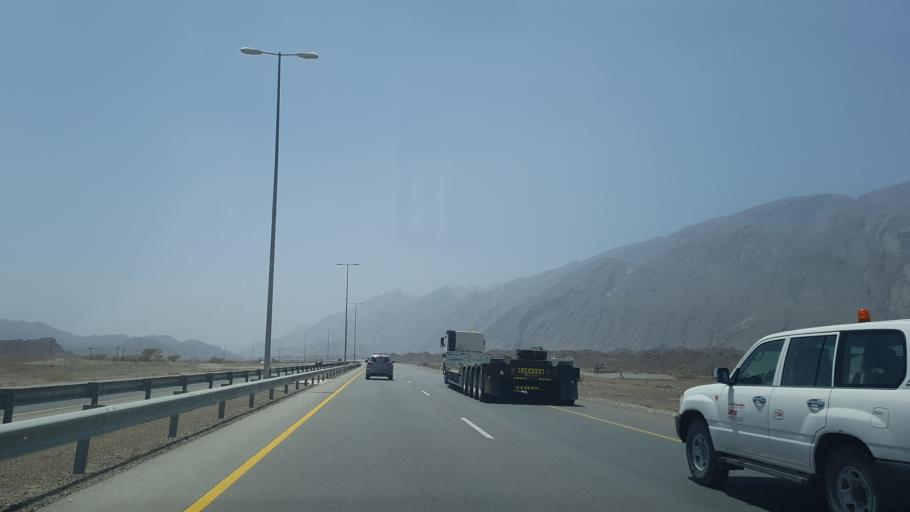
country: OM
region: Muhafazat ad Dakhiliyah
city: Sufalat Sama'il
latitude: 23.2334
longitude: 57.9063
